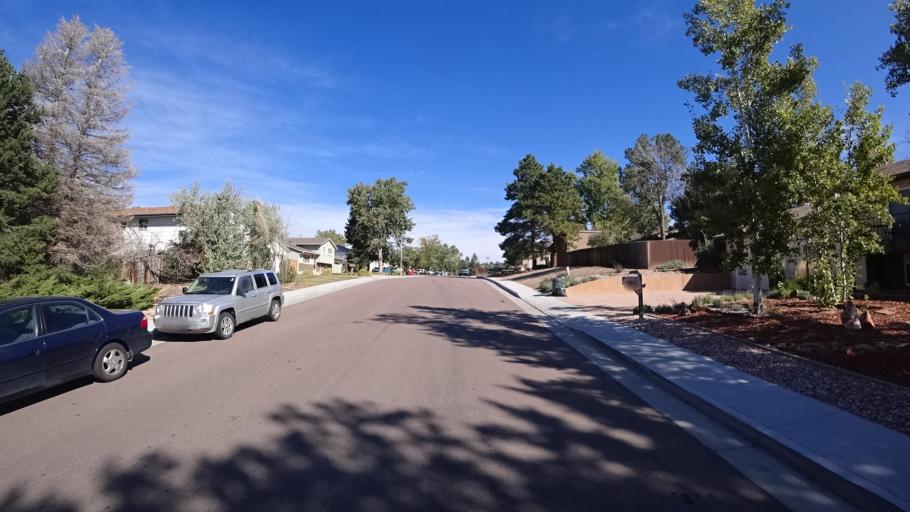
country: US
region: Colorado
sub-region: El Paso County
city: Colorado Springs
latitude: 38.9112
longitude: -104.7737
